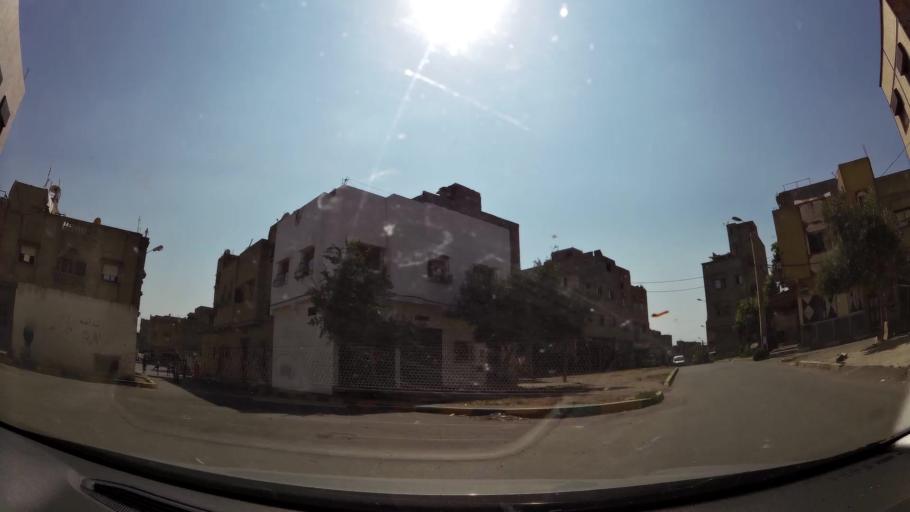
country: MA
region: Rabat-Sale-Zemmour-Zaer
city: Sale
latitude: 34.0687
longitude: -6.7702
